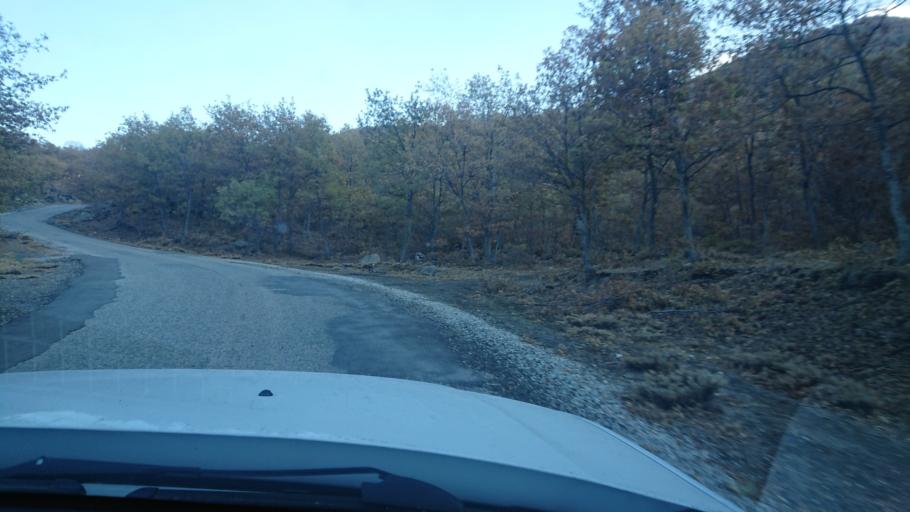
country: TR
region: Aksaray
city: Taspinar
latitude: 38.1666
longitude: 34.1947
